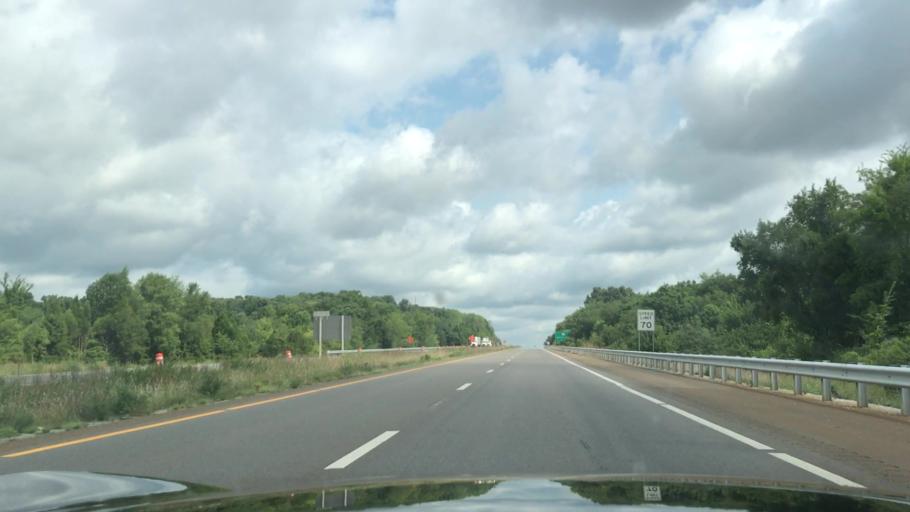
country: US
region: Kentucky
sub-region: Warren County
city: Bowling Green
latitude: 36.9623
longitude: -86.4978
